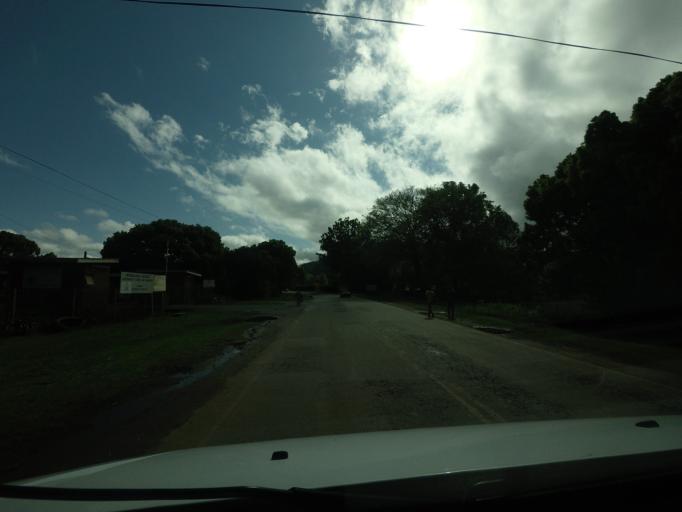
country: ZA
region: Mpumalanga
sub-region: Ehlanzeni District
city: Graksop
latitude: -25.0914
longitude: 30.7760
